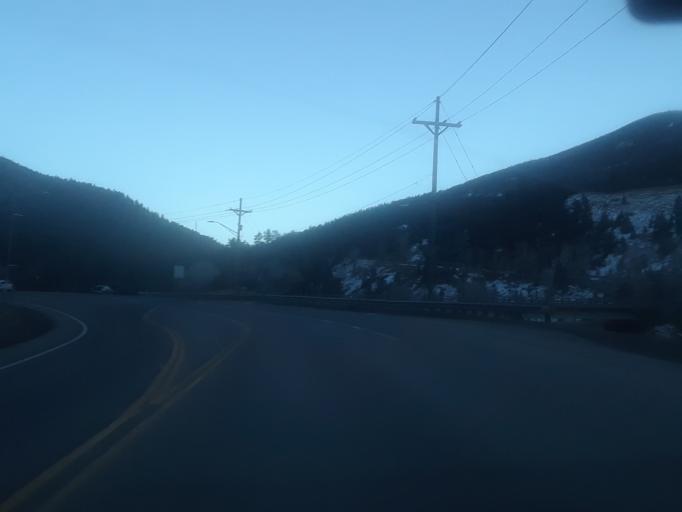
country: US
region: Colorado
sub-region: Clear Creek County
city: Idaho Springs
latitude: 39.7433
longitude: -105.4318
